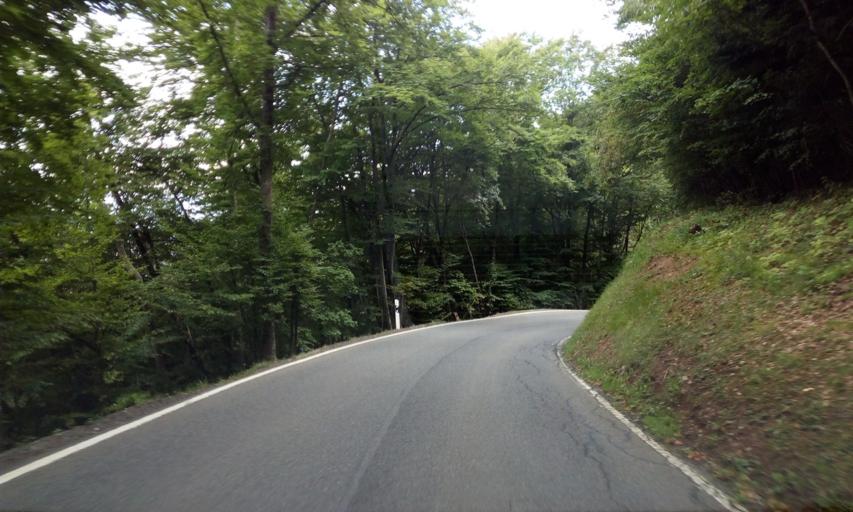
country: CH
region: Valais
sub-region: Monthey District
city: Vionnaz
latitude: 46.3103
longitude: 6.8825
